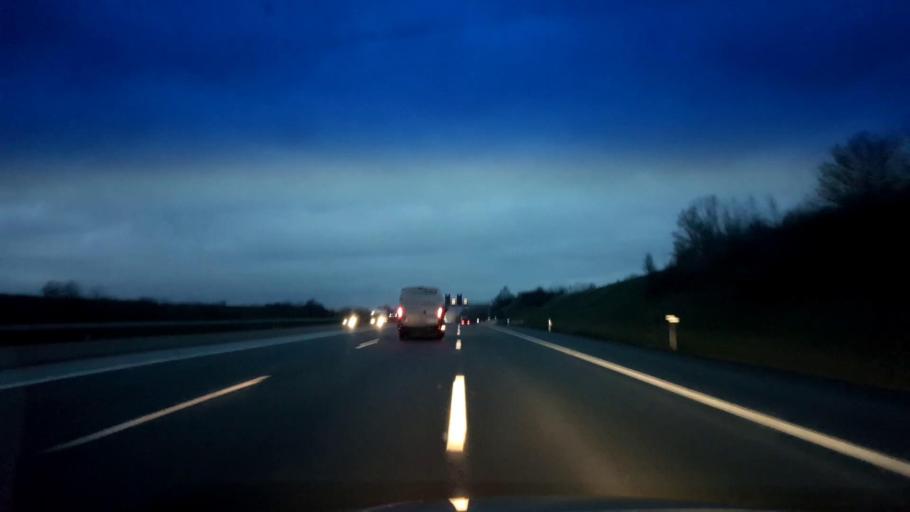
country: DE
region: Bavaria
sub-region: Upper Franconia
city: Bayreuth
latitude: 49.9456
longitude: 11.6069
